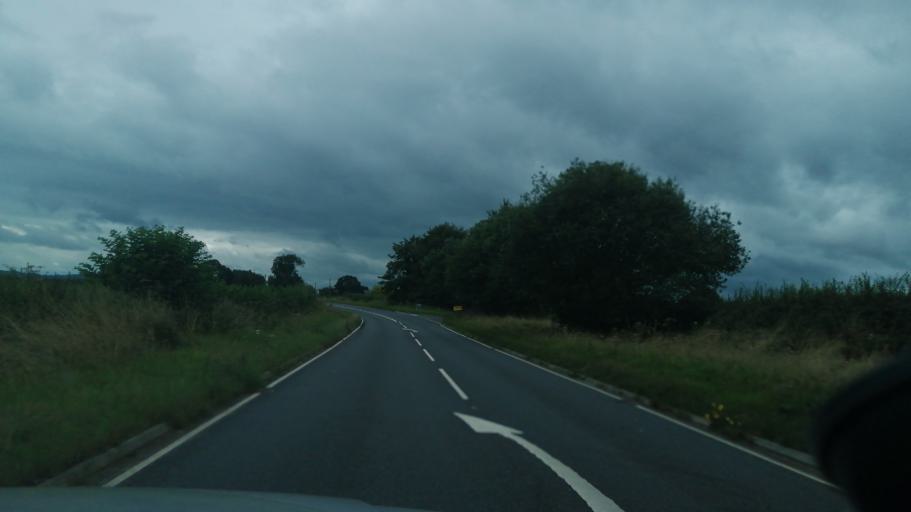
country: GB
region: England
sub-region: Herefordshire
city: Thruxton
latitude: 52.0093
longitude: -2.7901
